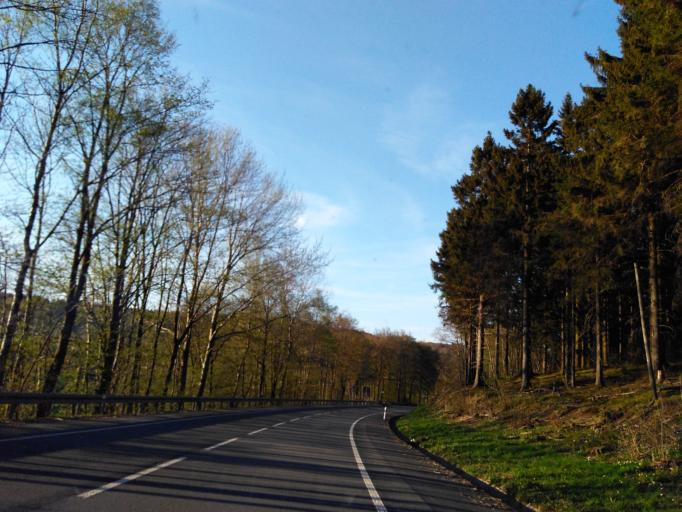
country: DE
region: North Rhine-Westphalia
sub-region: Regierungsbezirk Arnsberg
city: Herscheid
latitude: 51.1518
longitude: 7.7416
